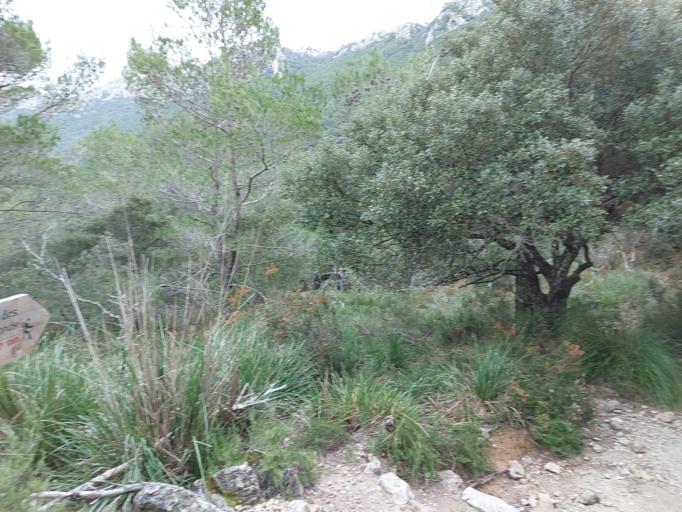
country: ES
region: Balearic Islands
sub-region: Illes Balears
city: Escorca
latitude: 39.7876
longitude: 2.8284
